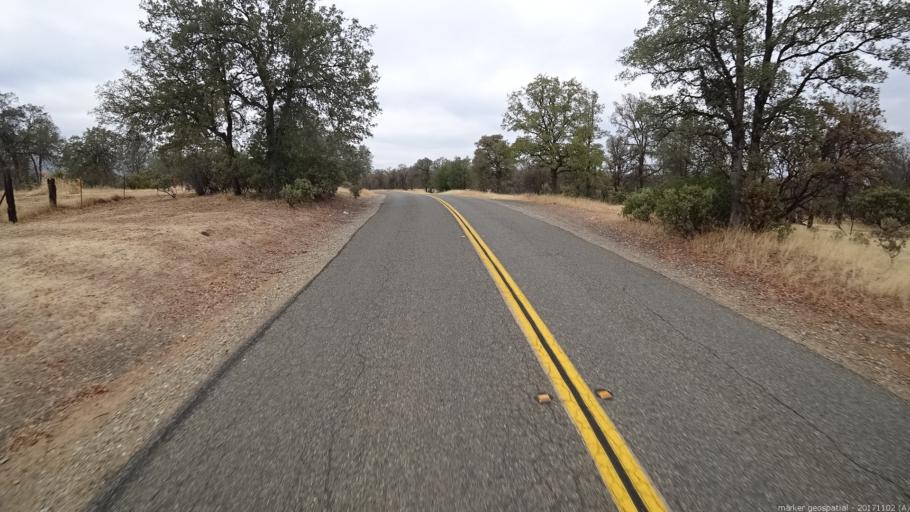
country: US
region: California
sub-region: Shasta County
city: Redding
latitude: 40.6243
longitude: -122.4310
